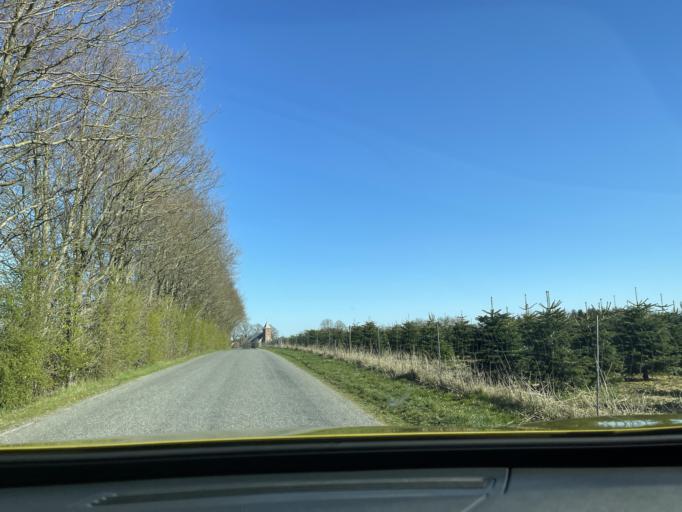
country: DK
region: Central Jutland
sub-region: Silkeborg Kommune
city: Kjellerup
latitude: 56.2459
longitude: 9.4829
